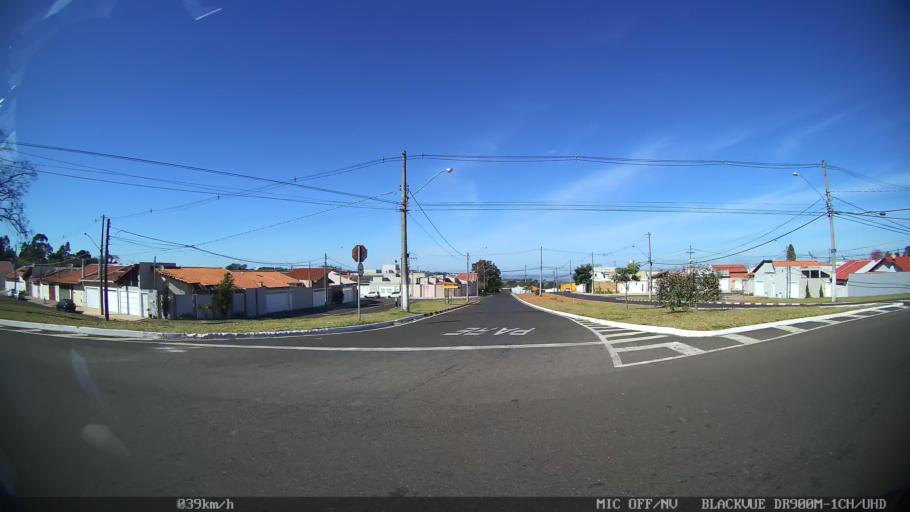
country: BR
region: Sao Paulo
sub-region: Franca
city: Franca
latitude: -20.5647
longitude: -47.3583
